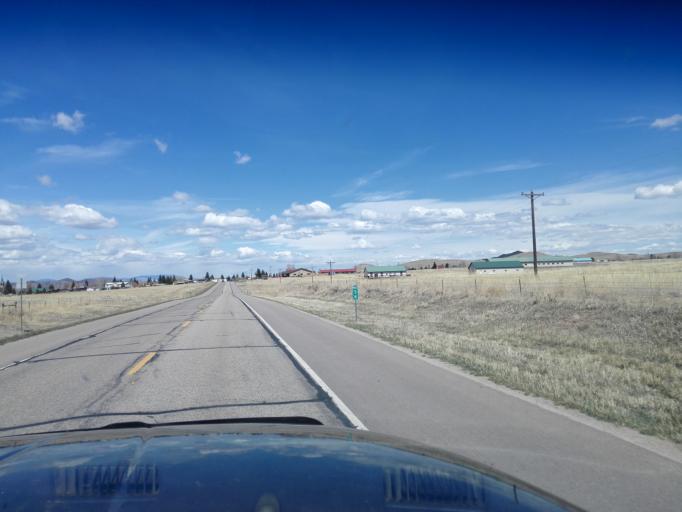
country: US
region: Colorado
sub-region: Custer County
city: Westcliffe
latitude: 38.1253
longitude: -105.4627
